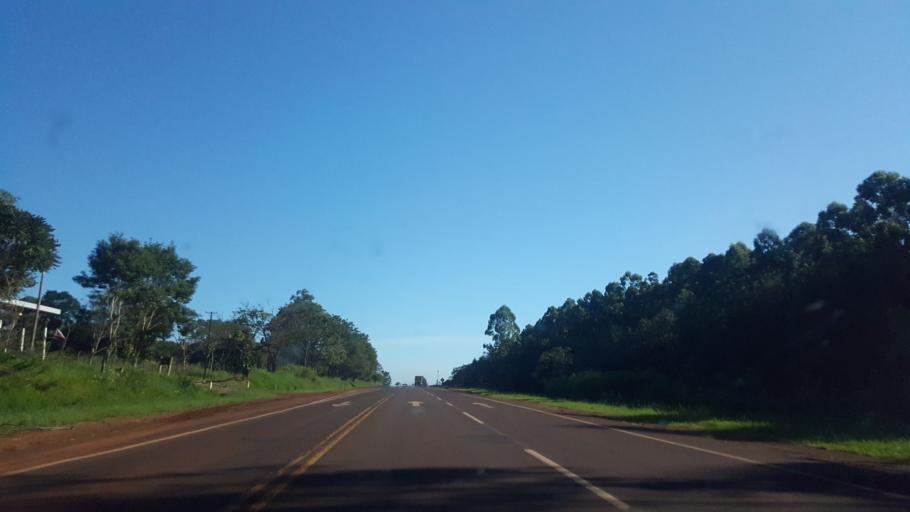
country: AR
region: Misiones
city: Puerto Esperanza
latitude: -26.1740
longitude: -54.5871
